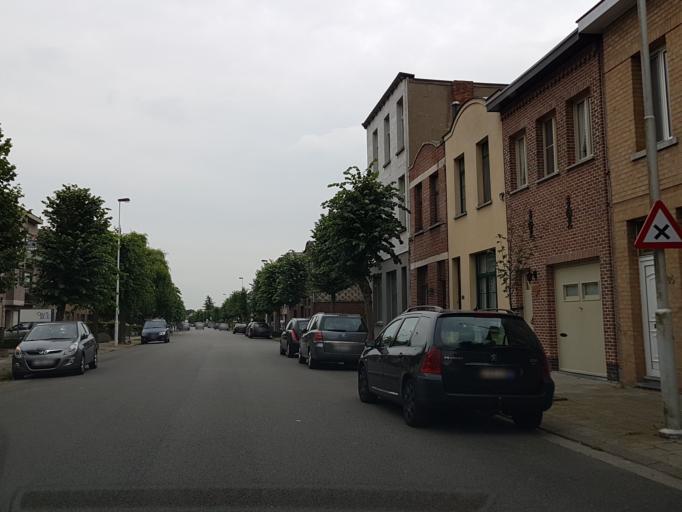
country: BE
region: Flanders
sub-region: Provincie Antwerpen
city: Borsbeek
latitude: 51.1974
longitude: 4.4740
